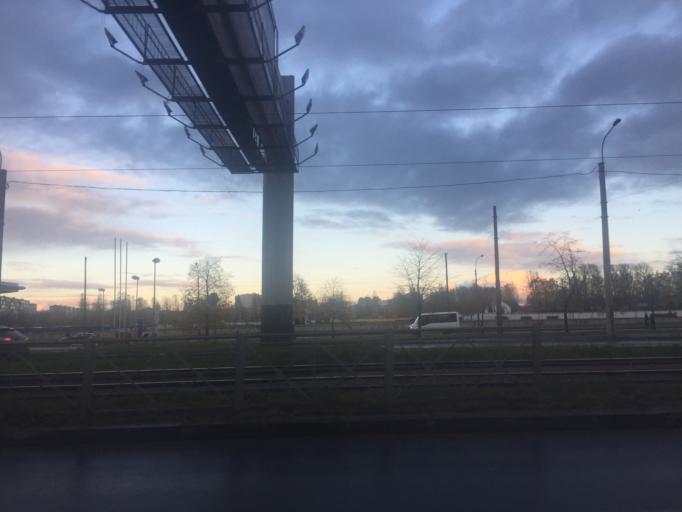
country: RU
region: St.-Petersburg
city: Obukhovo
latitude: 59.8888
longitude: 30.4638
